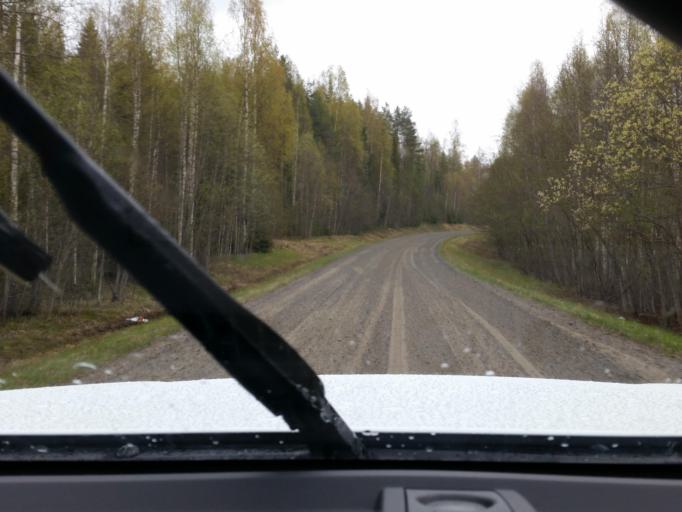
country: SE
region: Norrbotten
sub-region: Pitea Kommun
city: Norrfjarden
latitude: 65.6195
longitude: 21.4133
